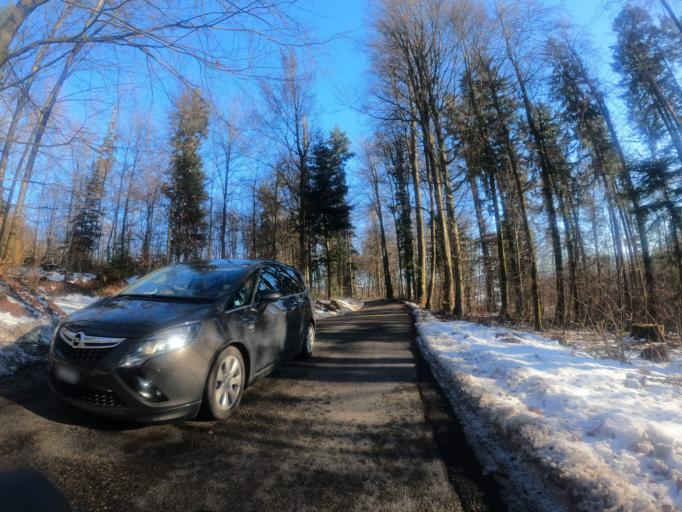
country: CH
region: Zurich
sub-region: Bezirk Affoltern
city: Hedingen
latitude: 47.2991
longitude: 8.4270
